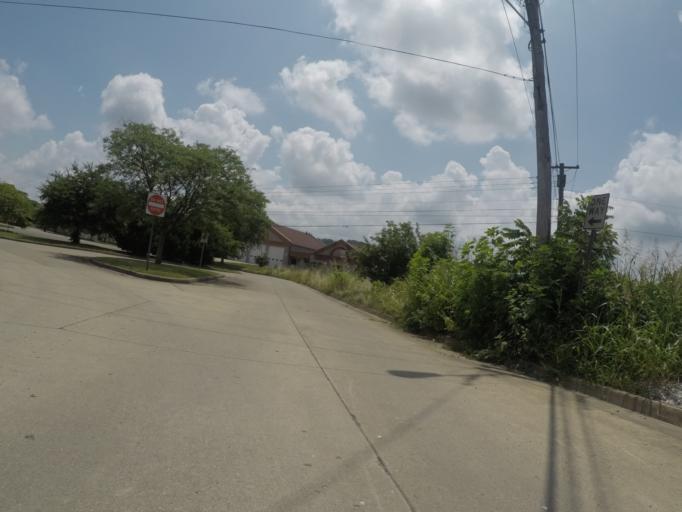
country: US
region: West Virginia
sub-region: Cabell County
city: Huntington
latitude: 38.4109
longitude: -82.4810
